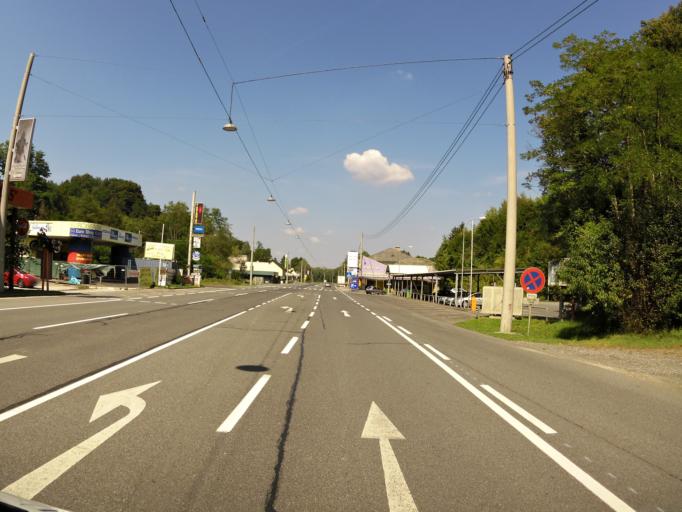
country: AT
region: Styria
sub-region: Politischer Bezirk Leibnitz
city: Spielfeld
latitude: 46.6992
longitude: 15.6367
